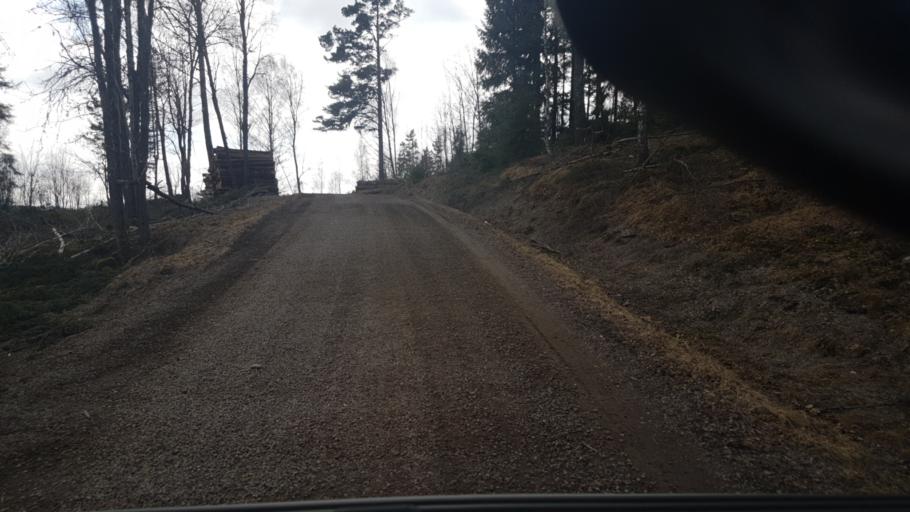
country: SE
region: Vaermland
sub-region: Eda Kommun
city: Amotfors
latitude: 59.8173
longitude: 12.4213
